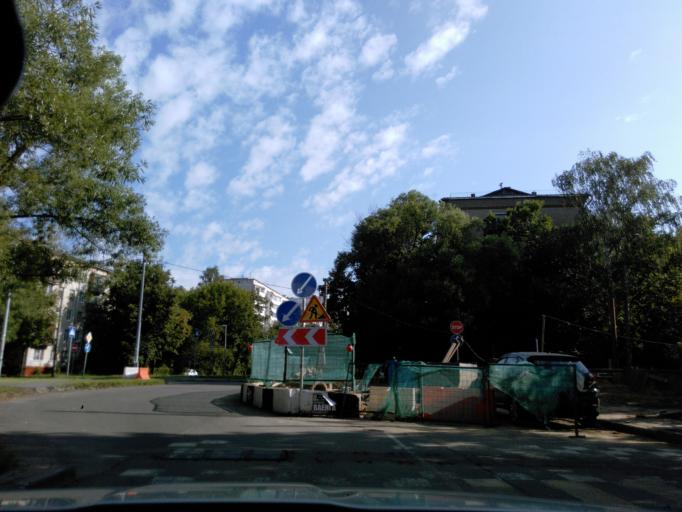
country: RU
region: Moskovskaya
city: Koptevo
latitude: 55.8312
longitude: 37.5266
